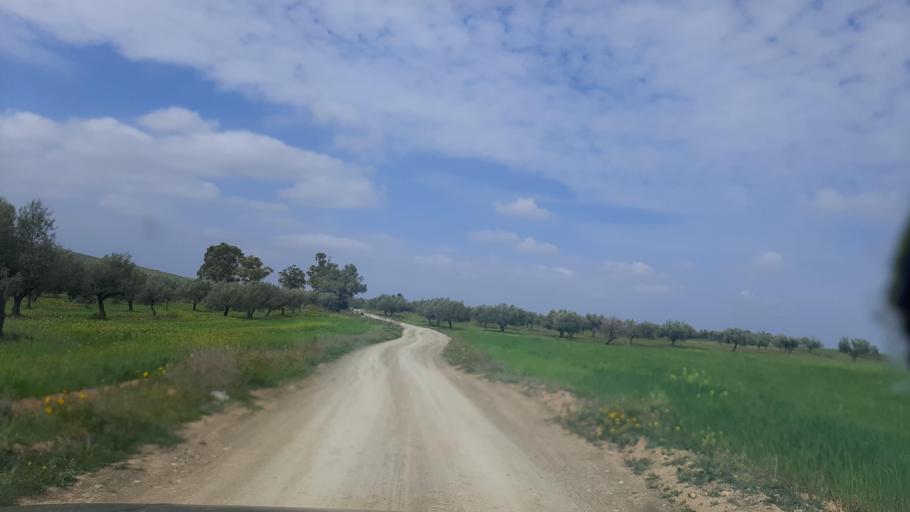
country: TN
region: Tunis
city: Oued Lill
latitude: 36.6883
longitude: 9.9958
